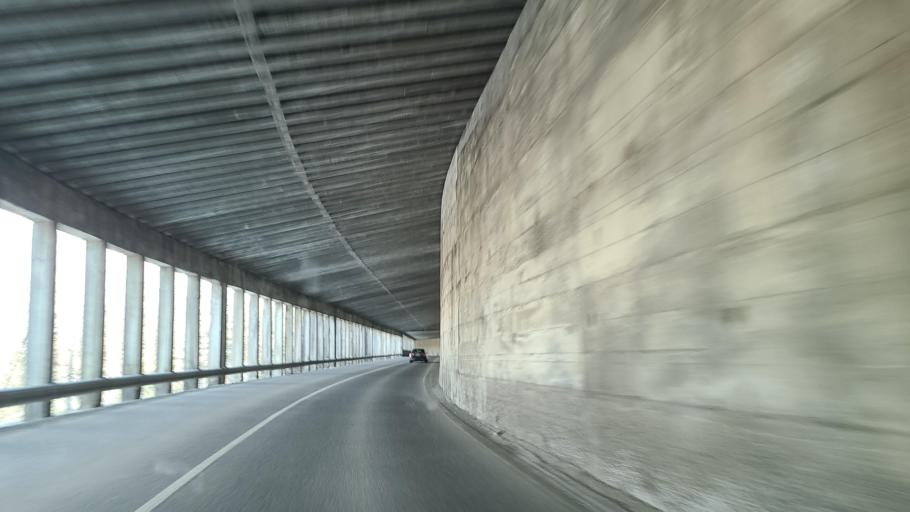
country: IT
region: Lombardy
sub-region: Provincia di Sondrio
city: Isolaccia
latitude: 46.4826
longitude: 10.2380
